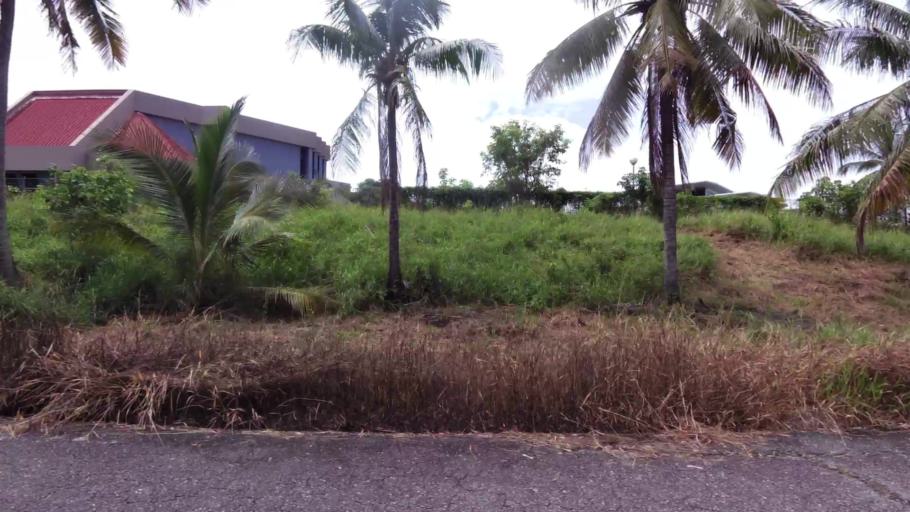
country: BN
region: Brunei and Muara
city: Bandar Seri Begawan
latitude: 4.9013
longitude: 114.9124
